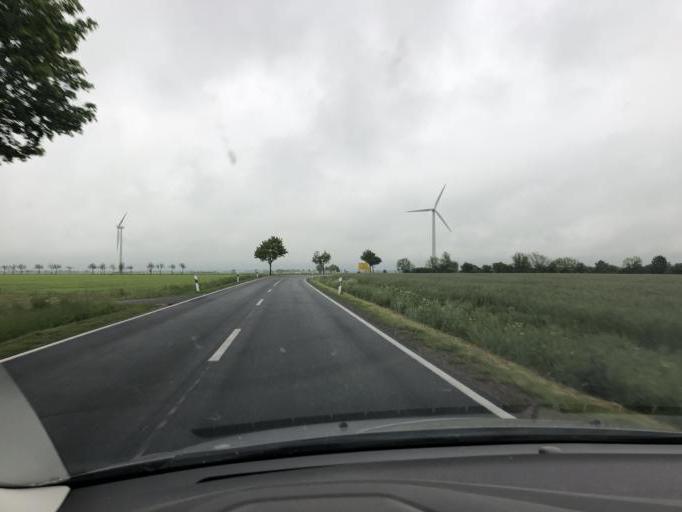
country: DE
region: Saxony
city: Zschortau
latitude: 51.5050
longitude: 12.3812
